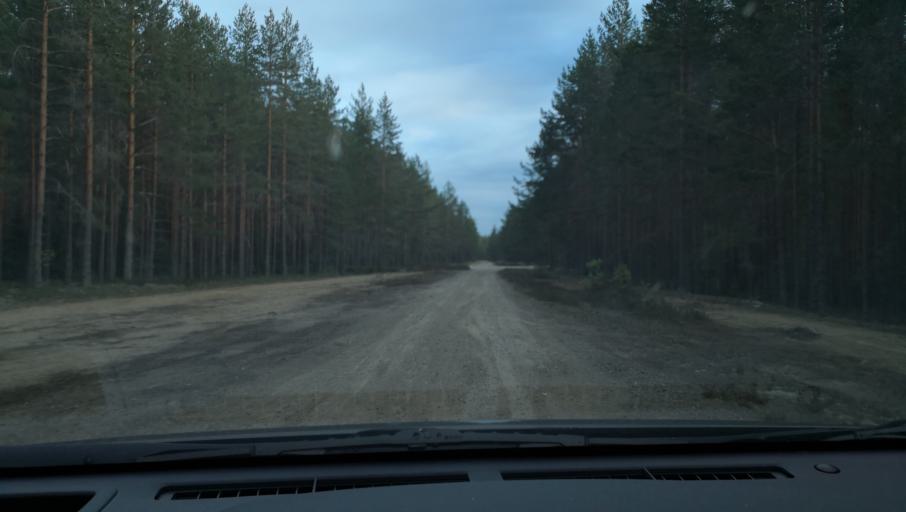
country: SE
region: Vaestmanland
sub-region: Skinnskattebergs Kommun
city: Skinnskatteberg
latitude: 59.8031
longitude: 15.4970
